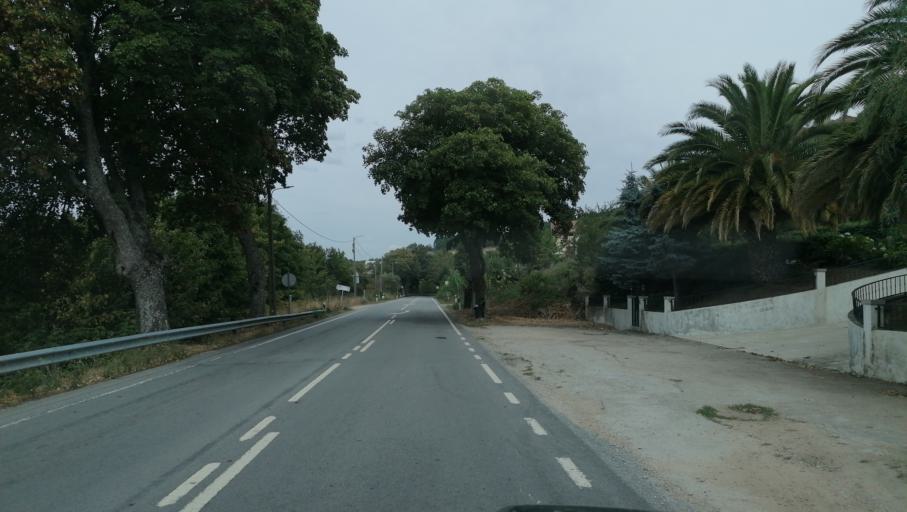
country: PT
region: Vila Real
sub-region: Vila Pouca de Aguiar
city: Vila Pouca de Aguiar
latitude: 41.5239
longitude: -7.6157
